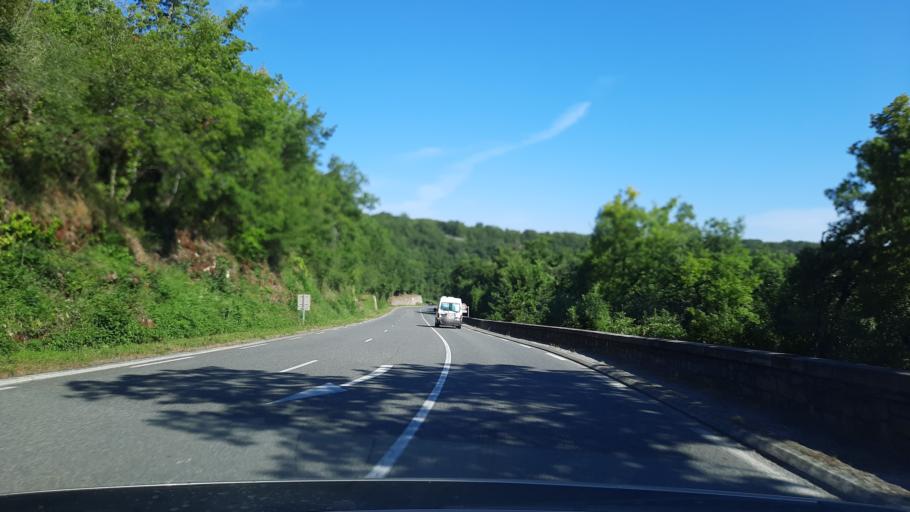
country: FR
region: Midi-Pyrenees
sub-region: Departement du Tarn-et-Garonne
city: Caylus
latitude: 44.2330
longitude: 1.7675
